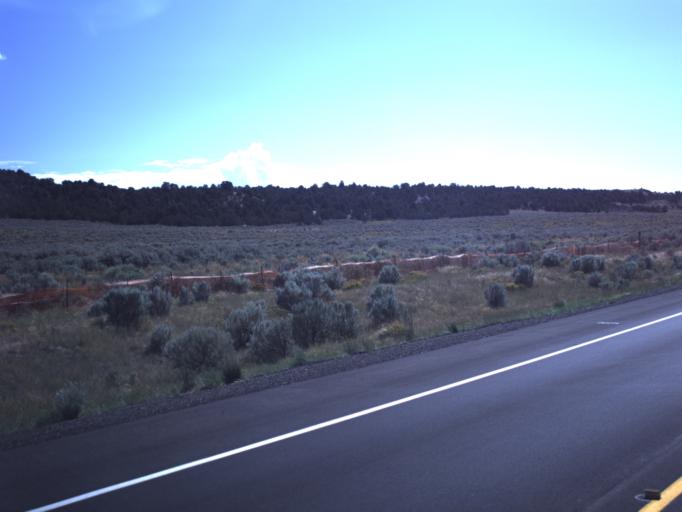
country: US
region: Utah
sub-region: Utah County
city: Genola
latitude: 39.9663
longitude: -112.2527
